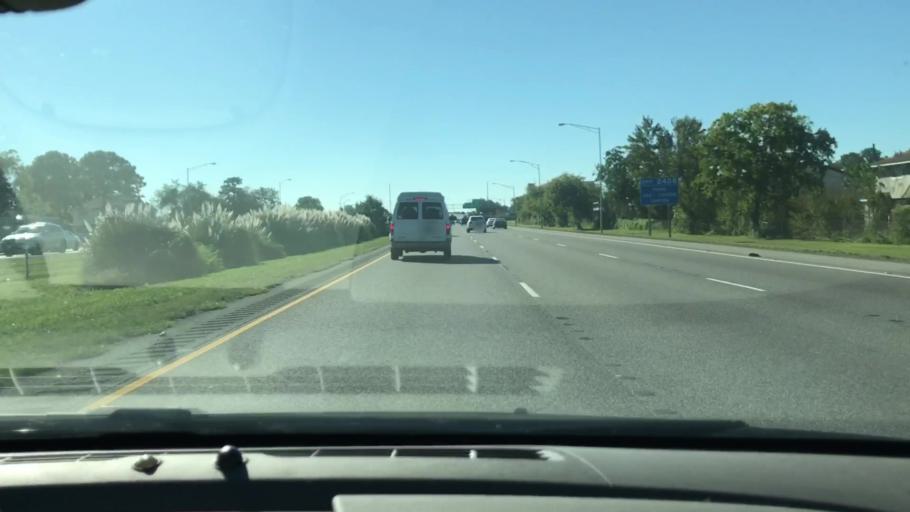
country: US
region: Louisiana
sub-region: Saint Bernard Parish
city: Arabi
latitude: 30.0166
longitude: -90.0137
